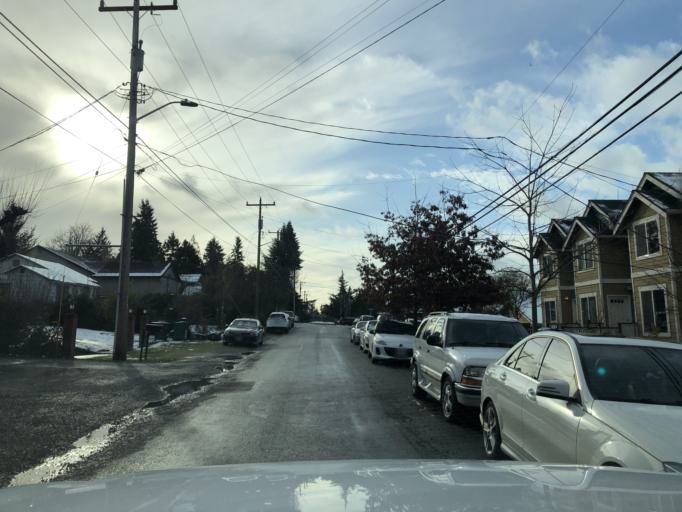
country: US
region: Washington
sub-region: King County
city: Lake Forest Park
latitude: 47.7309
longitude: -122.2910
